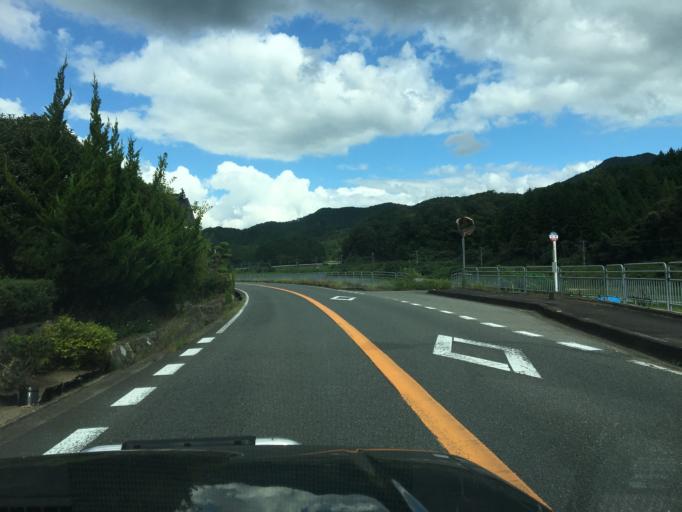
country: JP
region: Kyoto
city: Fukuchiyama
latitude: 35.3236
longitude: 134.9017
